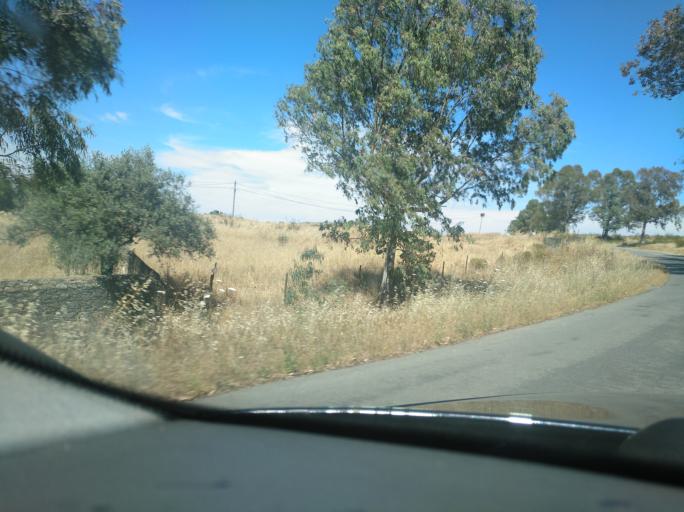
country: PT
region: Beja
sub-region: Almodovar
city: Almodovar
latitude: 37.5408
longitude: -7.9667
